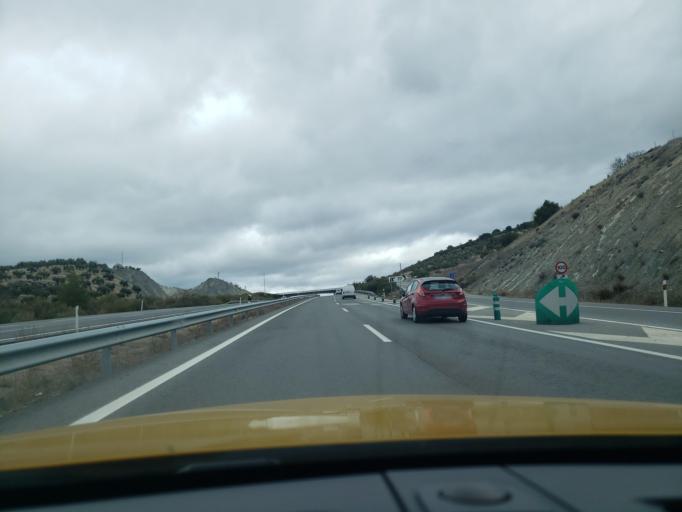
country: ES
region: Andalusia
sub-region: Provincia de Jaen
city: Noalejo
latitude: 37.5290
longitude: -3.6365
